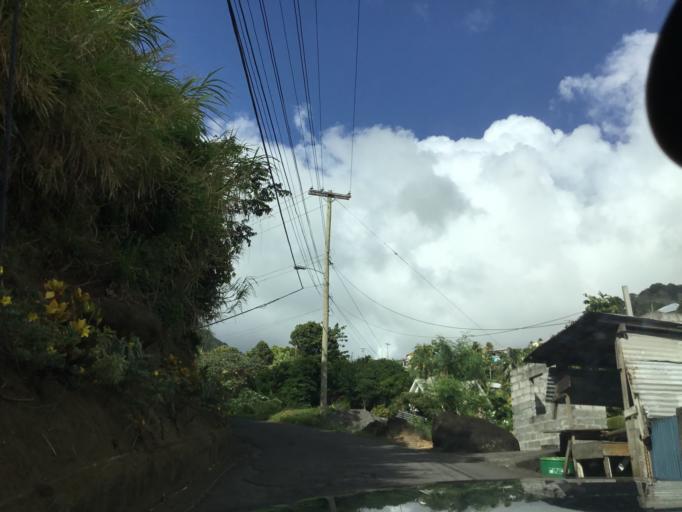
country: VC
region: Saint George
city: Kingstown
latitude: 13.1672
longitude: -61.2203
